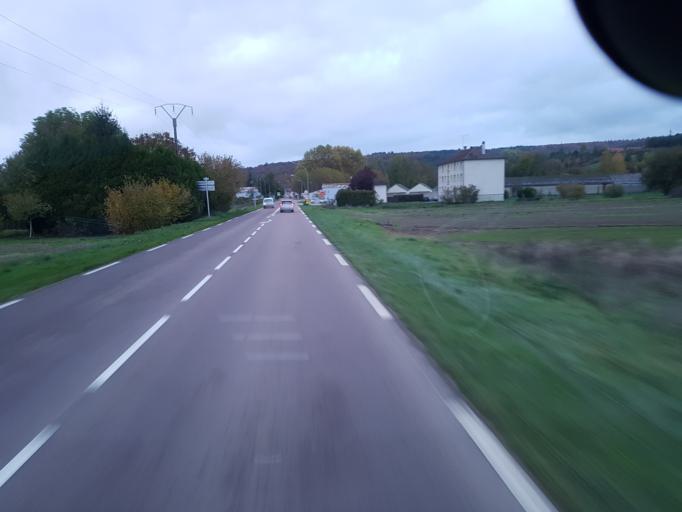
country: FR
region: Champagne-Ardenne
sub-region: Departement de l'Aube
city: Mussy-sur-Seine
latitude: 47.9721
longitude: 4.5007
